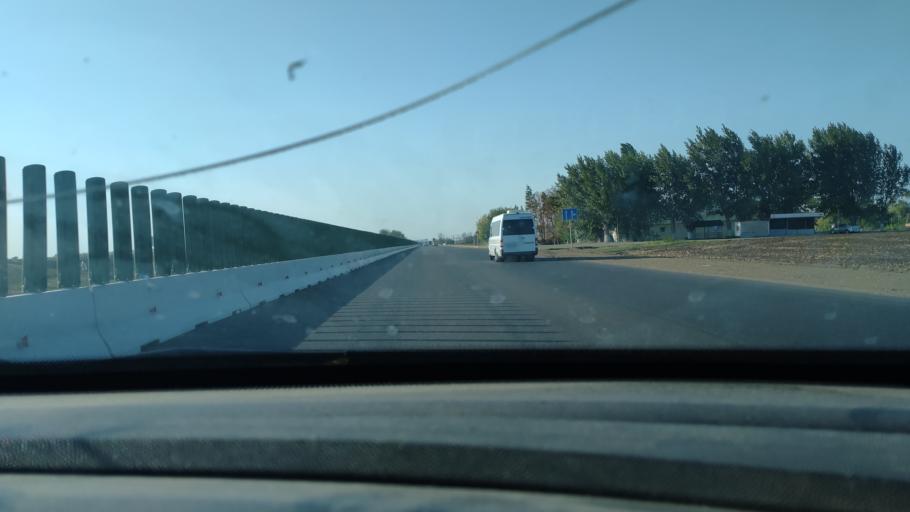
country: RU
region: Krasnodarskiy
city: Medvedovskaya
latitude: 45.4756
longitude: 38.9727
